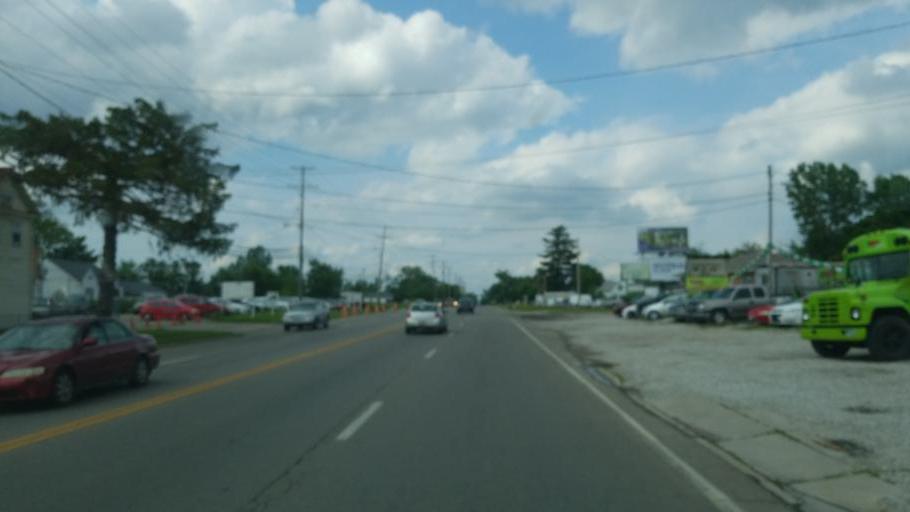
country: US
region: Ohio
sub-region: Franklin County
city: Minerva Park
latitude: 40.0380
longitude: -82.9522
